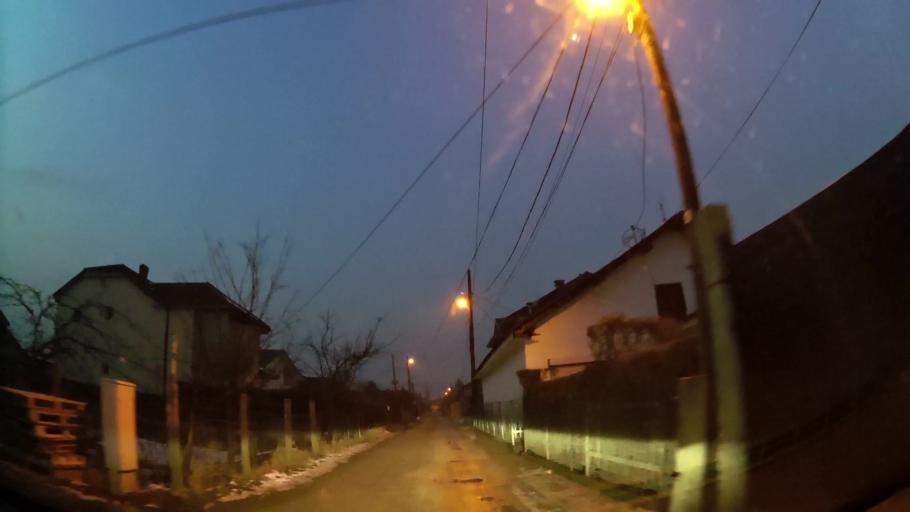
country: MK
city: Creshevo
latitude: 42.0002
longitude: 21.5134
